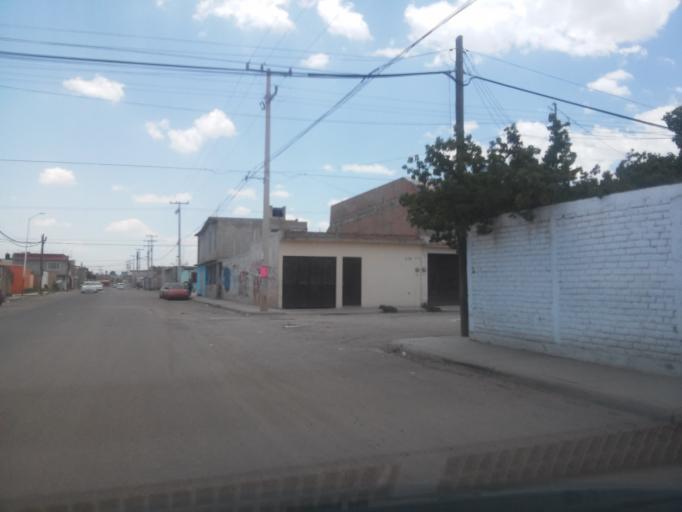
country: MX
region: Durango
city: Victoria de Durango
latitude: 24.0608
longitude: -104.6282
